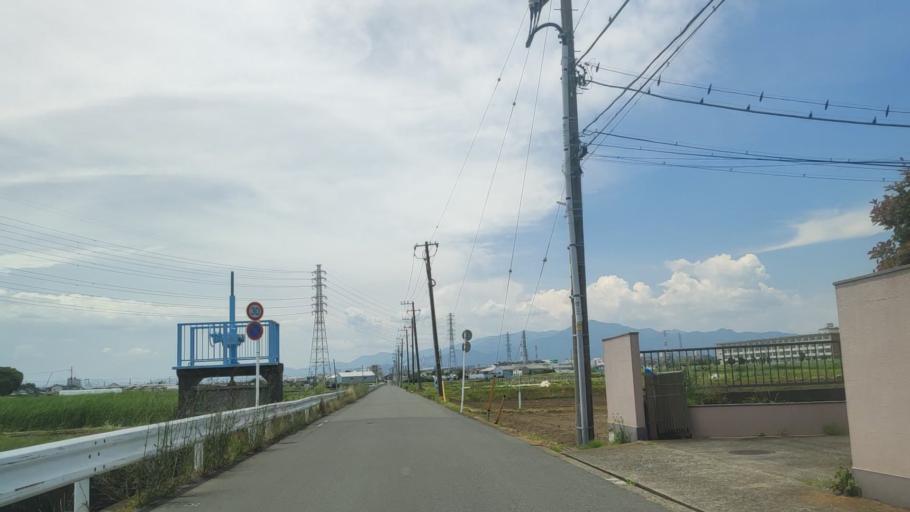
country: JP
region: Kanagawa
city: Chigasaki
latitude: 35.3561
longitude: 139.3904
